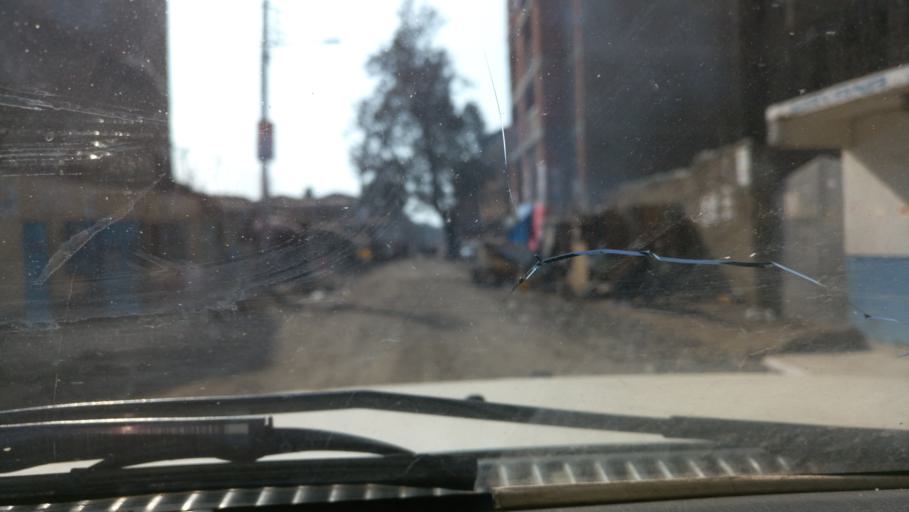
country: KE
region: Nairobi Area
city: Pumwani
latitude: -1.2666
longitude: 36.8516
